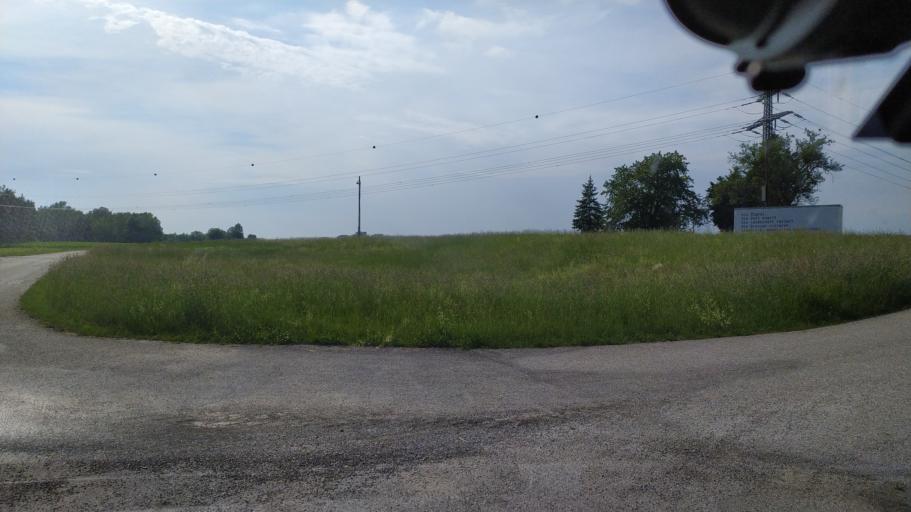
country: AT
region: Lower Austria
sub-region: Politischer Bezirk Amstetten
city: Zeillern
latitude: 48.1904
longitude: 14.7607
